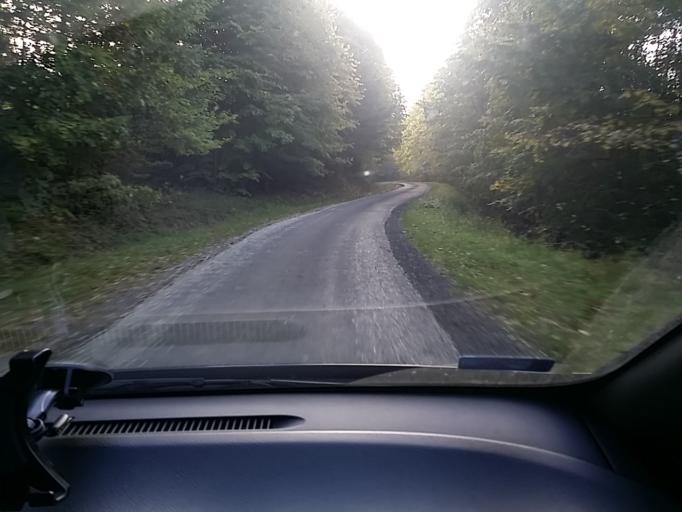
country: HU
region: Somogy
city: Kaposmero
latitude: 46.2524
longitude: 17.7538
